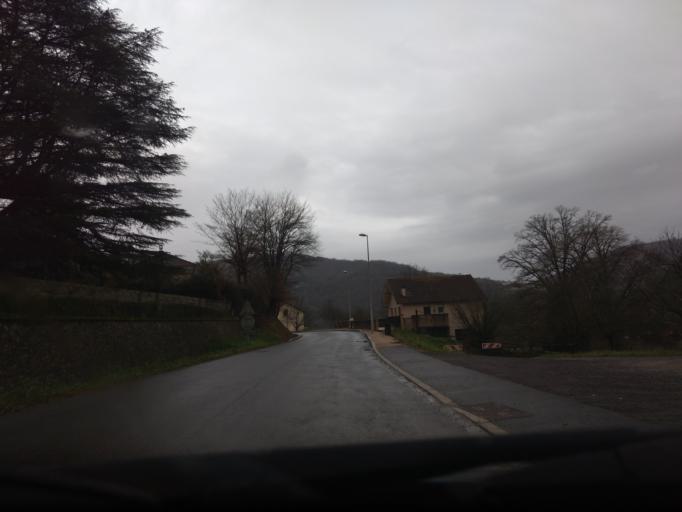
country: FR
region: Midi-Pyrenees
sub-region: Departement de l'Aveyron
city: Livinhac-le-Haut
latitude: 44.5959
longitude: 2.2297
